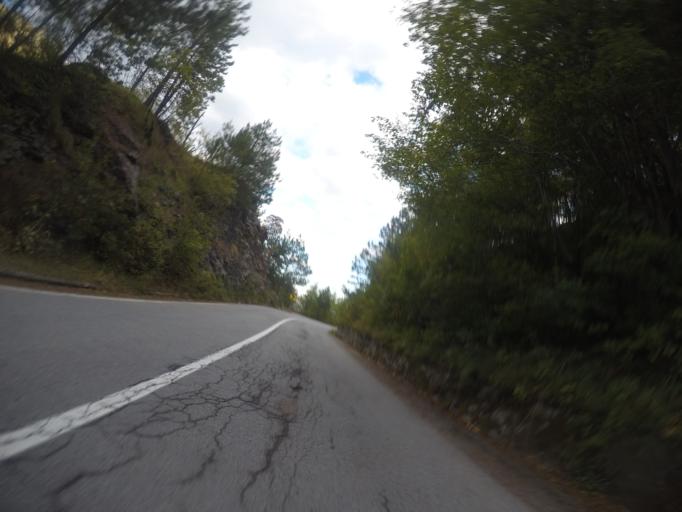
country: ME
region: Mojkovac
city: Mojkovac
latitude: 43.0047
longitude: 19.4345
